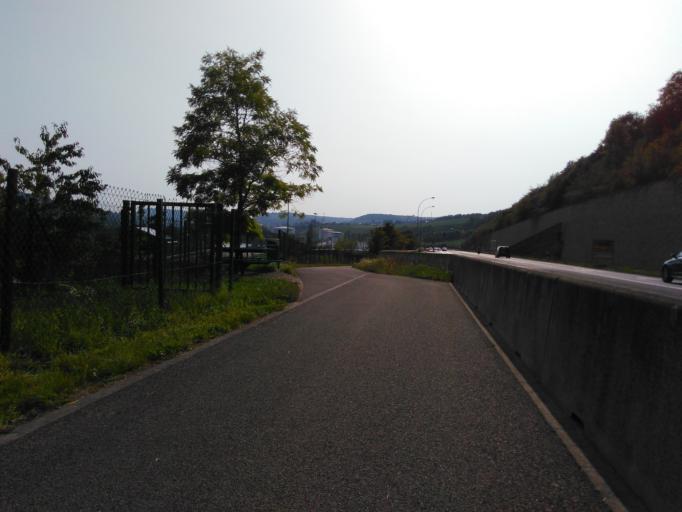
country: DE
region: Rheinland-Pfalz
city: Temmels
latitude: 49.6949
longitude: 6.4653
